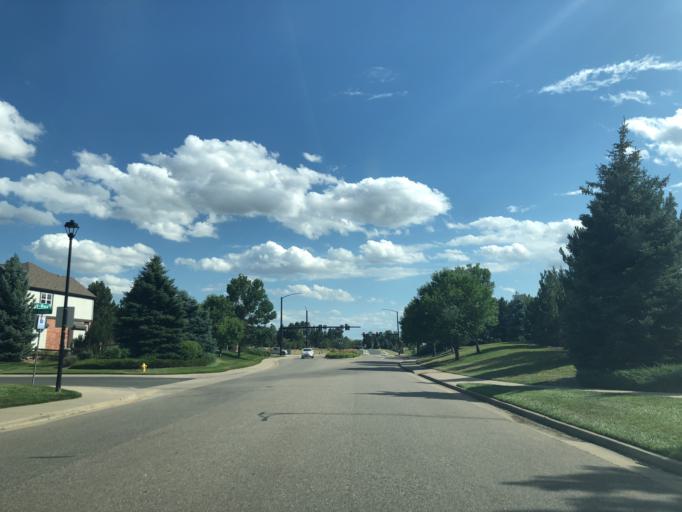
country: US
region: Colorado
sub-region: Arapahoe County
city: Dove Valley
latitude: 39.5964
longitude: -104.7779
